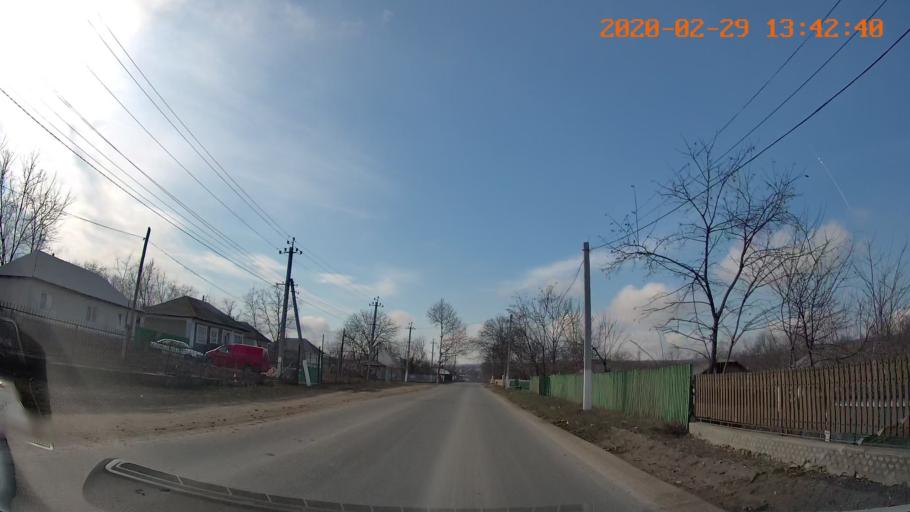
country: MD
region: Floresti
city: Leninskiy
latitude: 47.8408
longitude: 28.5442
